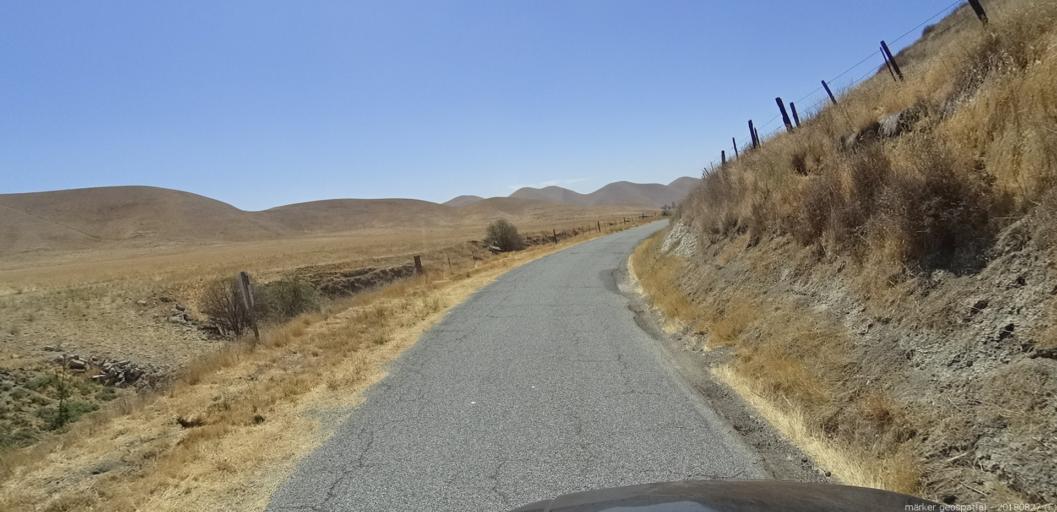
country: US
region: California
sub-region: Monterey County
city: King City
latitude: 36.1132
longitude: -120.8751
